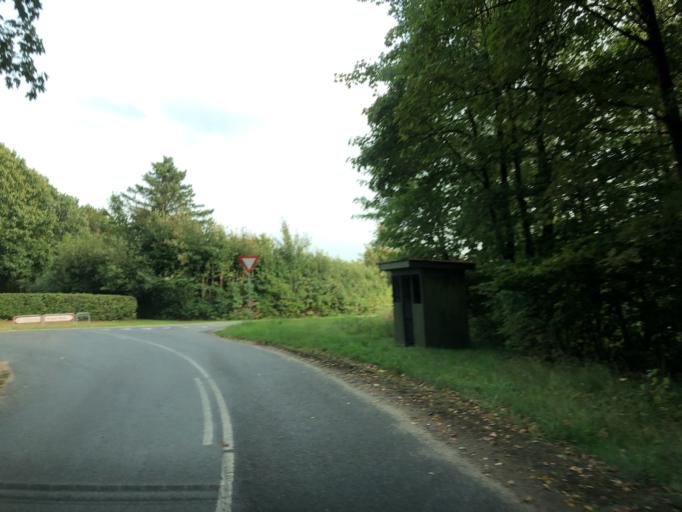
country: DK
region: Central Jutland
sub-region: Ringkobing-Skjern Kommune
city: Videbaek
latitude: 56.1120
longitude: 8.7000
